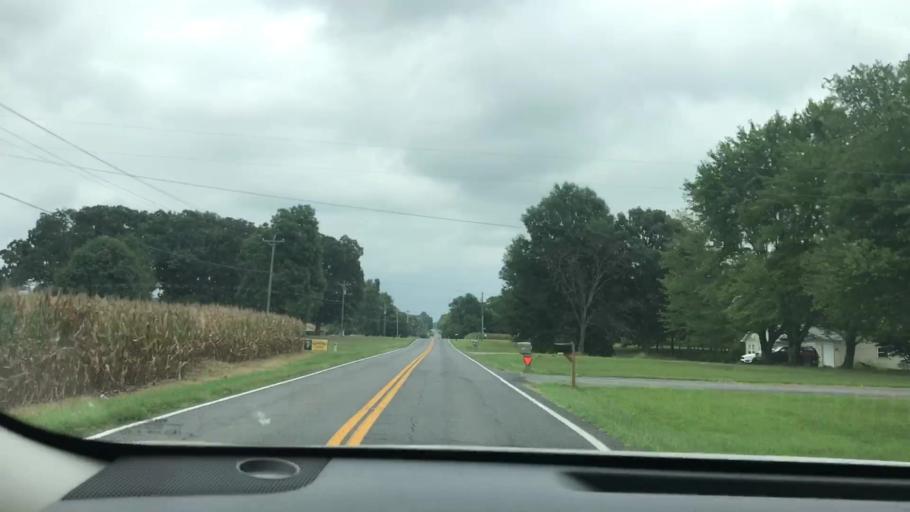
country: US
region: Kentucky
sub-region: Calloway County
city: Murray
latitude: 36.5806
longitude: -88.2609
